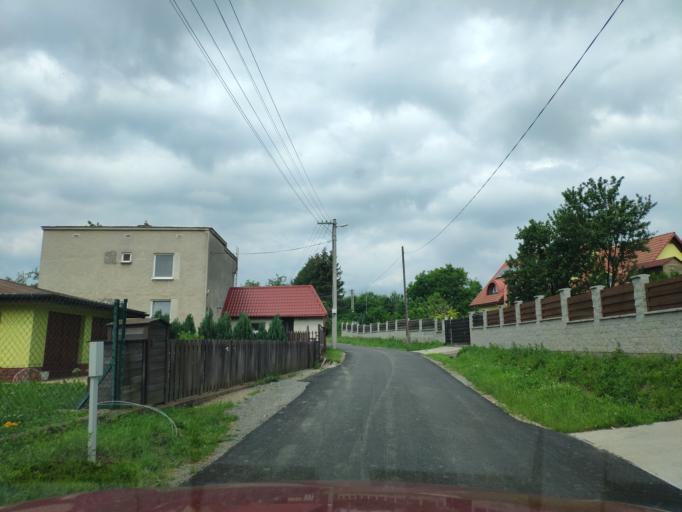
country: SK
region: Kosicky
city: Kosice
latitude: 48.8014
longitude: 21.3004
